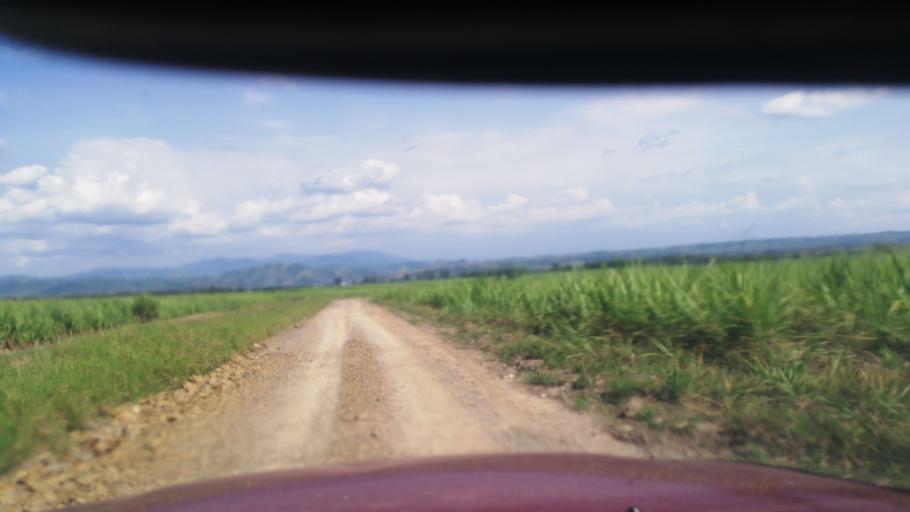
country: CO
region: Risaralda
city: La Virginia
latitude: 4.8917
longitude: -75.9217
